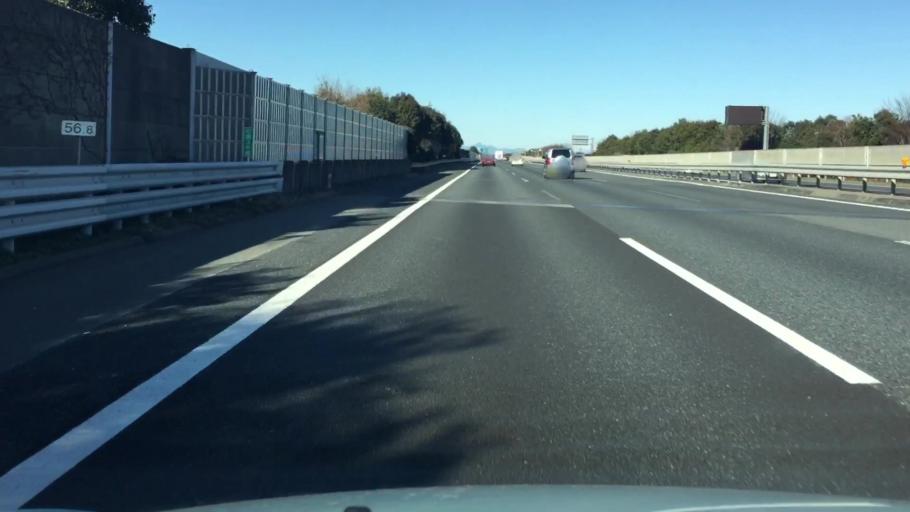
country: JP
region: Saitama
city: Yorii
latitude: 36.1271
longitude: 139.2434
